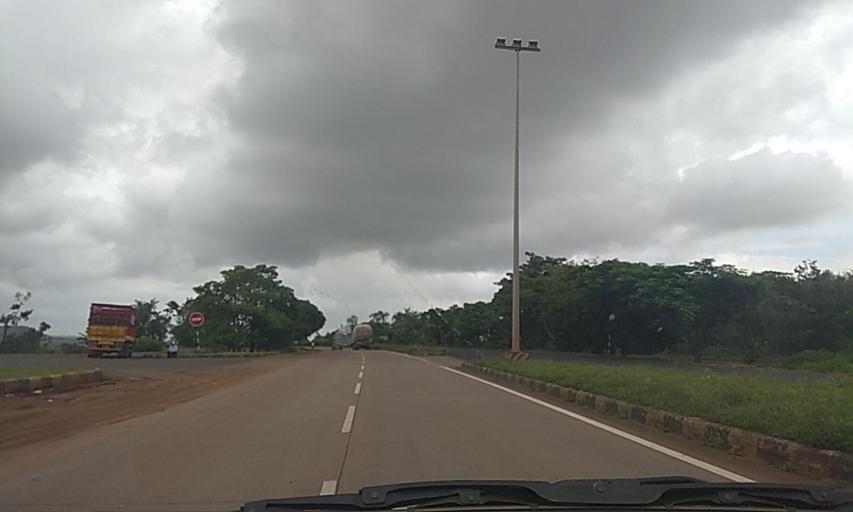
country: IN
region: Karnataka
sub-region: Belgaum
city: Sankeshwar
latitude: 16.2738
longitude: 74.4575
